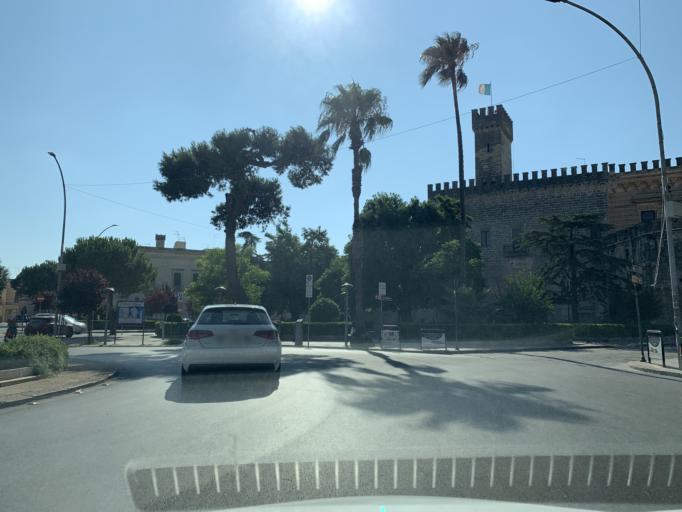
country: IT
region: Apulia
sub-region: Provincia di Lecce
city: Nardo
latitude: 40.1758
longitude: 18.0319
